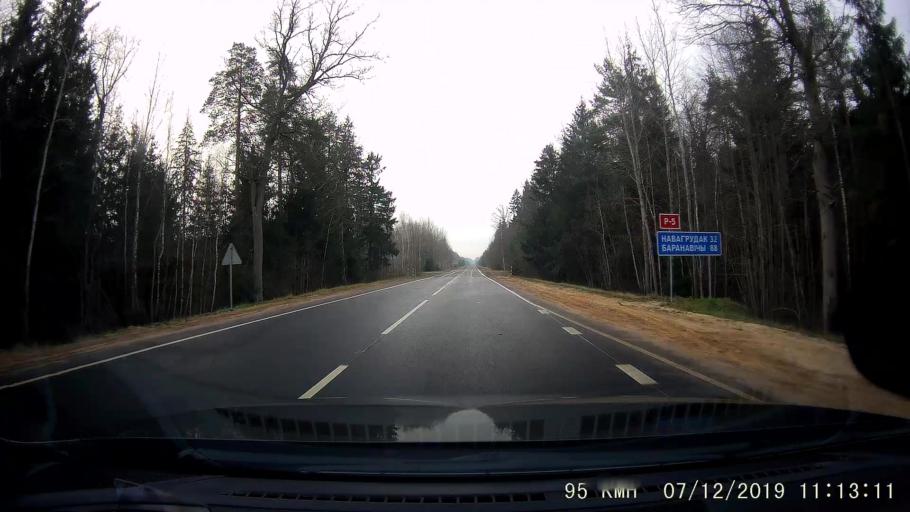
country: BY
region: Grodnenskaya
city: Iwye
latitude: 53.8779
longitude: 25.7397
